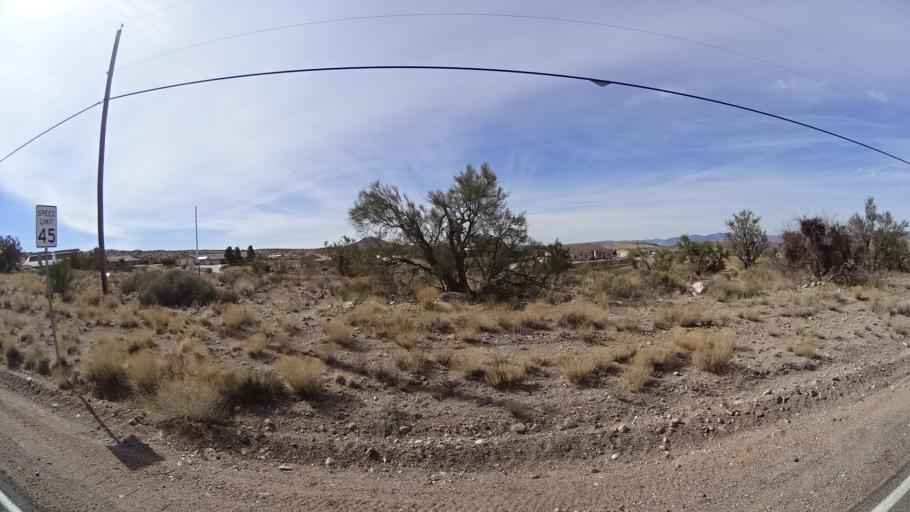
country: US
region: Arizona
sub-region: Mohave County
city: Kingman
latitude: 35.1729
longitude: -113.9839
